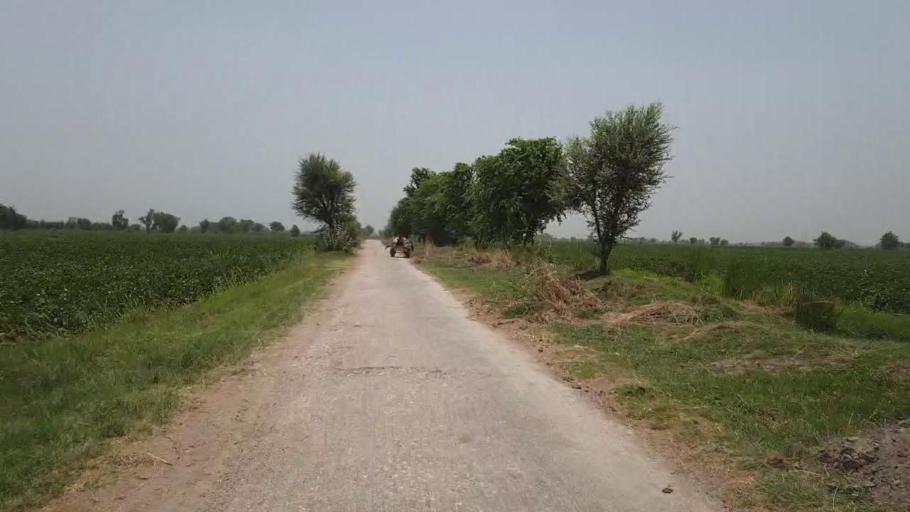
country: PK
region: Sindh
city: Tando Mittha Khan
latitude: 26.0722
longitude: 69.2161
